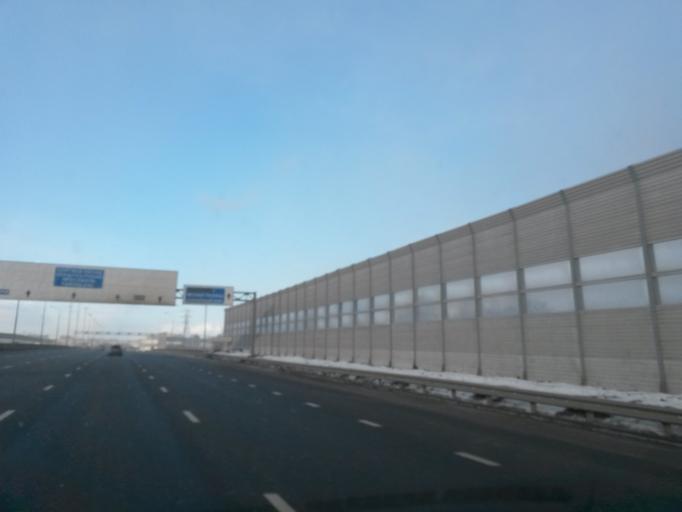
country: RU
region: Moskovskaya
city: Bolshevo
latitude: 55.9581
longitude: 37.8326
